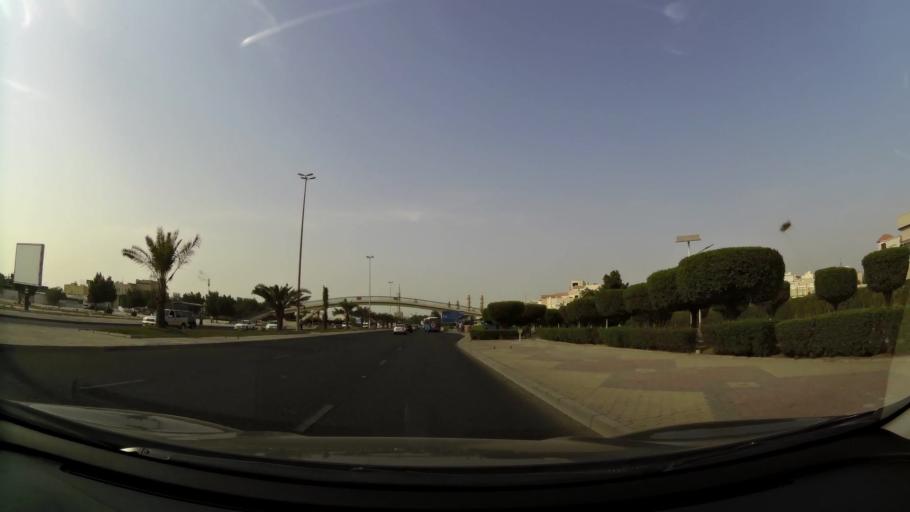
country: KW
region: Al Asimah
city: Ash Shamiyah
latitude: 29.3284
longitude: 47.9556
